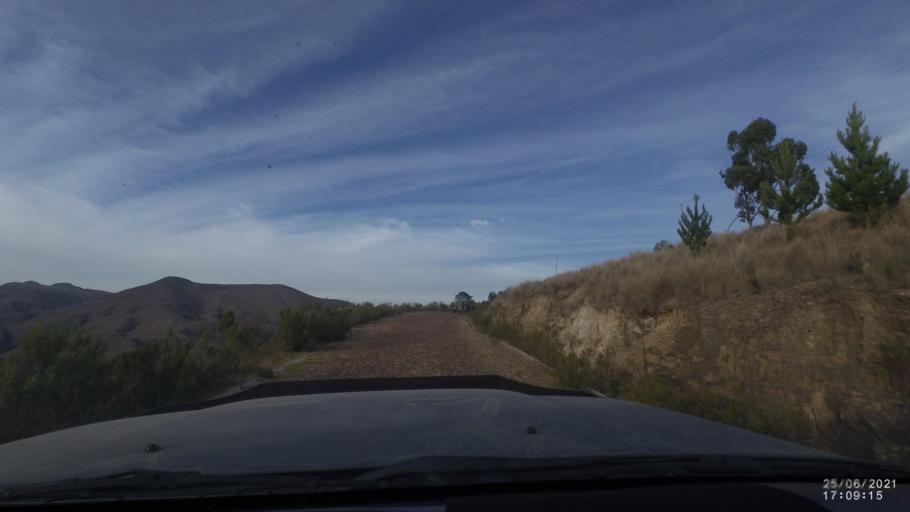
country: BO
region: Cochabamba
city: Arani
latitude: -17.8373
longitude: -65.7069
